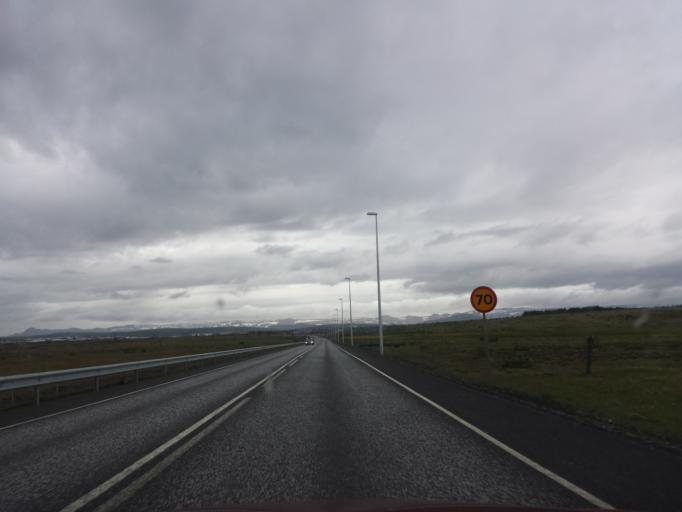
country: IS
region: Capital Region
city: Alftanes
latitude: 64.0962
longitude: -22.0010
